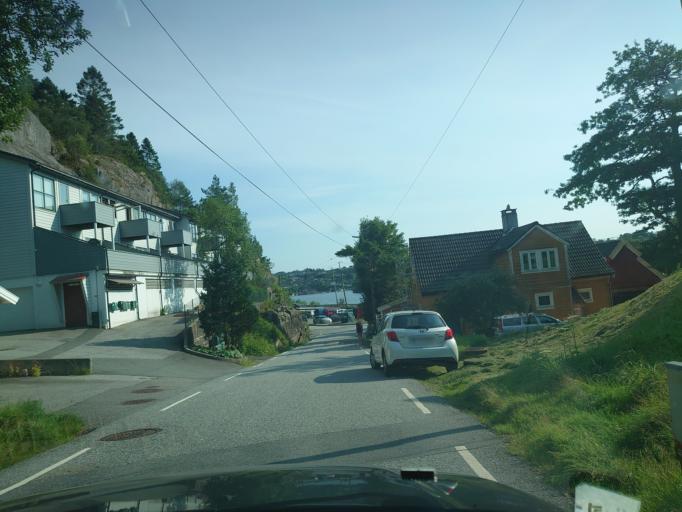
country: NO
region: Hordaland
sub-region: Bergen
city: Ytrebygda
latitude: 60.3265
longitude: 5.2809
